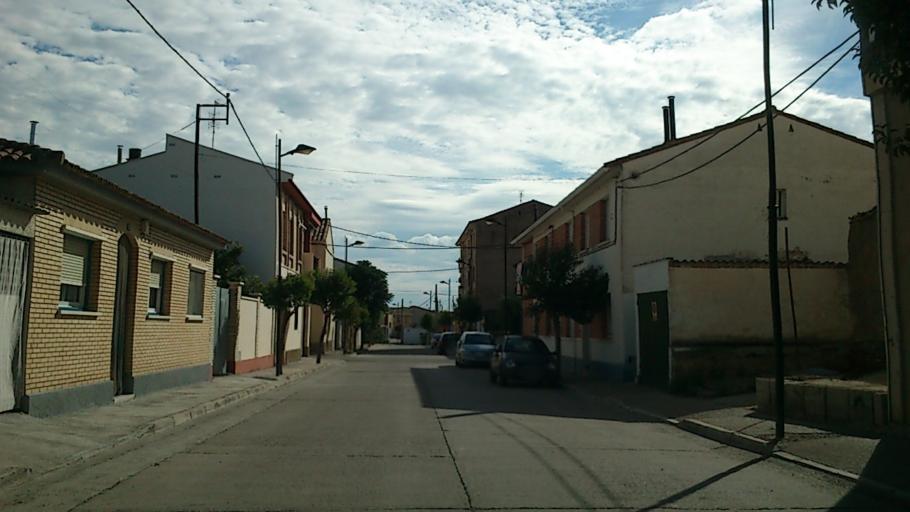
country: ES
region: Aragon
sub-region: Provincia de Zaragoza
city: San Mateo de Gallego
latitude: 41.8304
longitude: -0.7652
